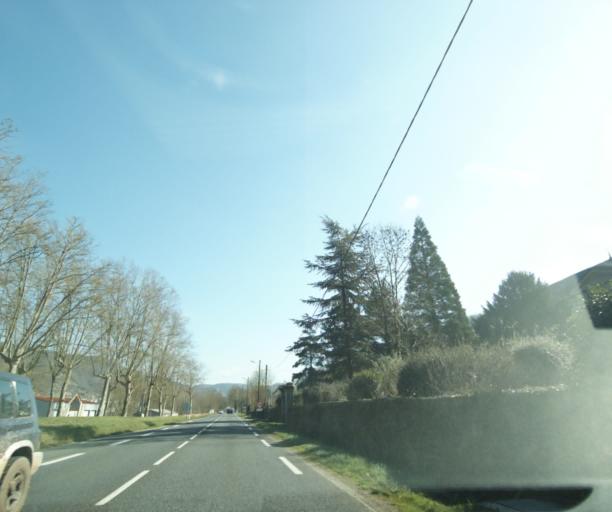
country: FR
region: Midi-Pyrenees
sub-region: Departement de l'Aveyron
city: Saint-Affrique
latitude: 43.9553
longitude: 2.8575
